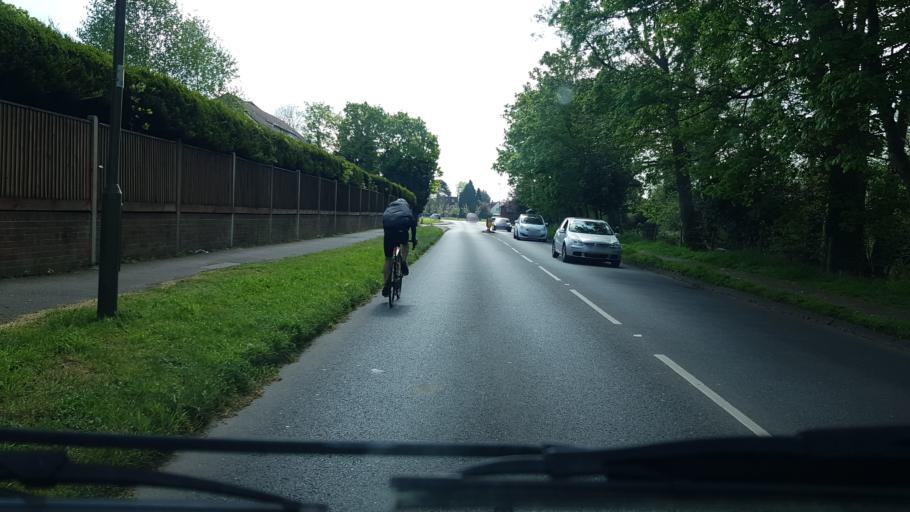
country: GB
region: England
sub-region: Surrey
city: Cobham
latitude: 51.3266
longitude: -0.4038
